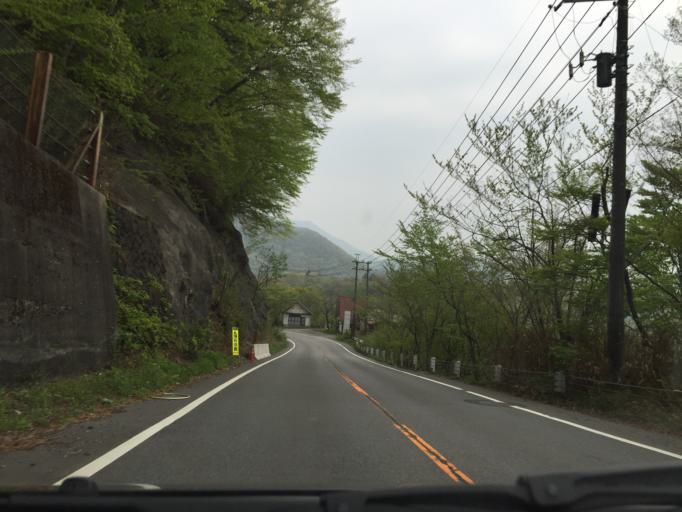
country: JP
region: Tochigi
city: Nikko
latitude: 36.9168
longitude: 139.6960
